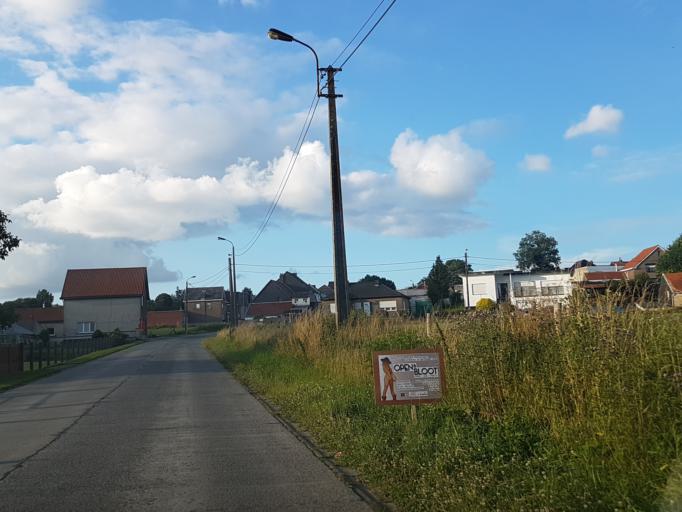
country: BE
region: Flanders
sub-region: Provincie Vlaams-Brabant
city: Opwijk
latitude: 50.9427
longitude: 4.1382
